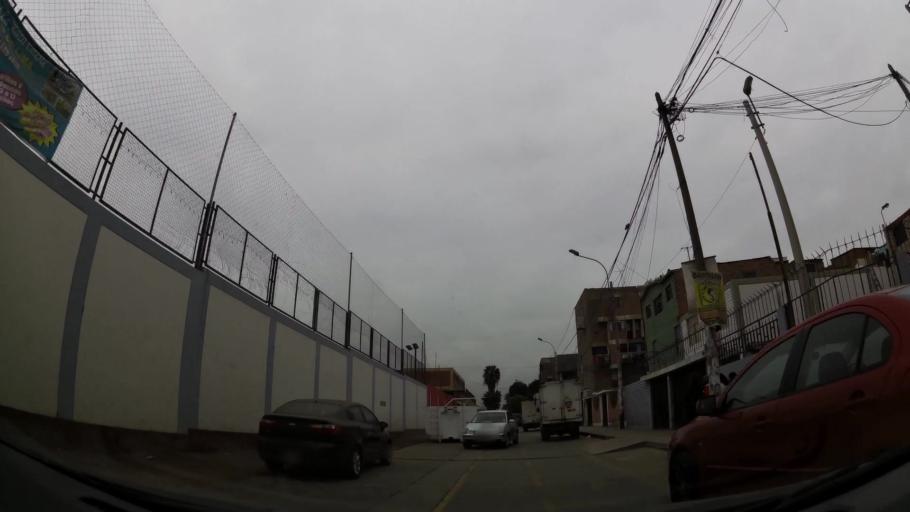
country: PE
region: Lima
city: Lima
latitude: -12.0528
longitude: -77.0697
